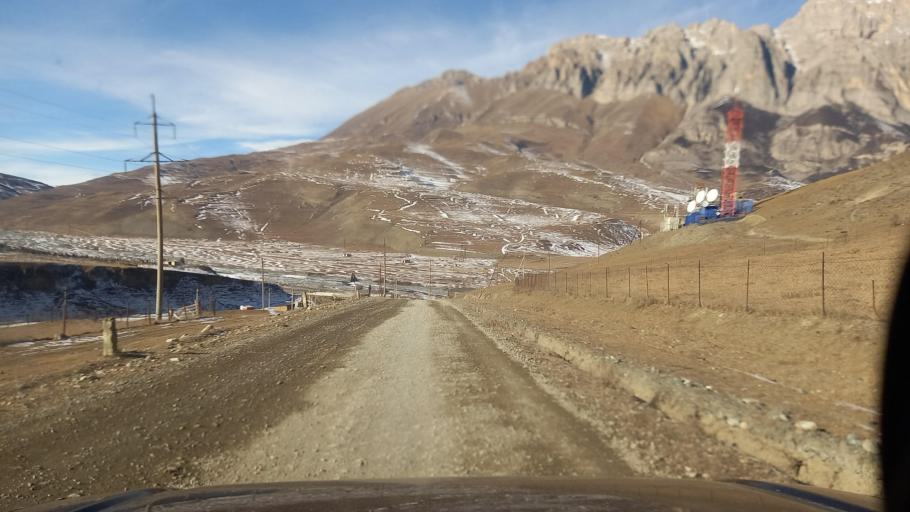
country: RU
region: North Ossetia
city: Verkhniy Fiagdon
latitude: 42.8391
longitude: 44.4491
